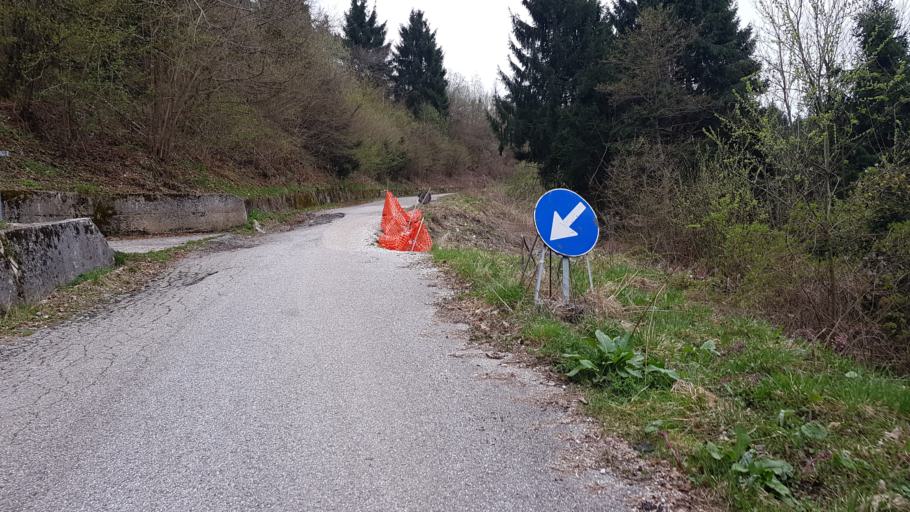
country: IT
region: Friuli Venezia Giulia
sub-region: Provincia di Udine
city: Faedis
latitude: 46.1932
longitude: 13.3618
